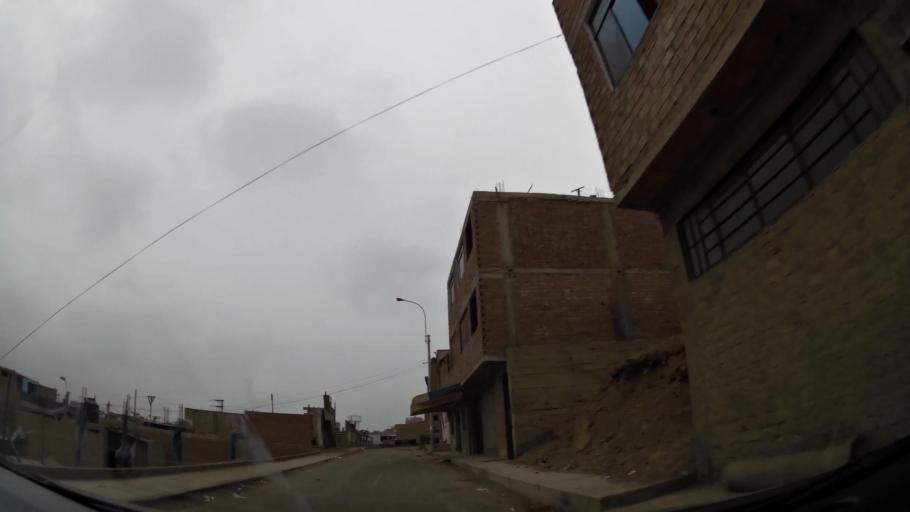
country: PE
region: Lima
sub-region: Lima
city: Surco
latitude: -12.1878
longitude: -76.9787
